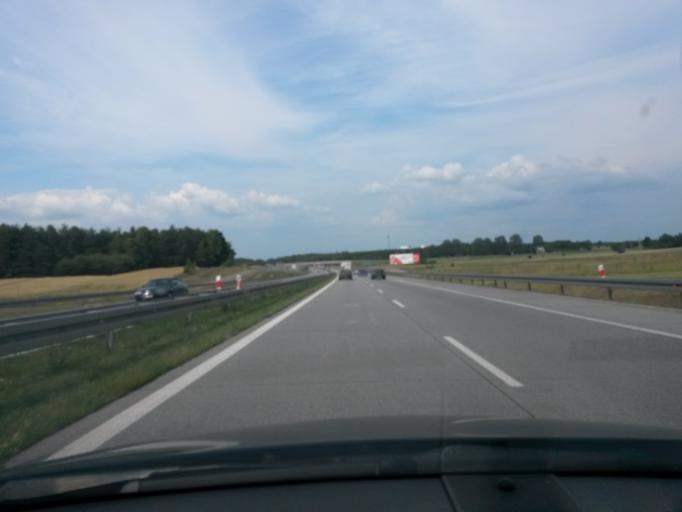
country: PL
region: Lodz Voivodeship
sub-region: Powiat tomaszowski
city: Czerniewice
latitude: 51.6891
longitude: 20.2062
